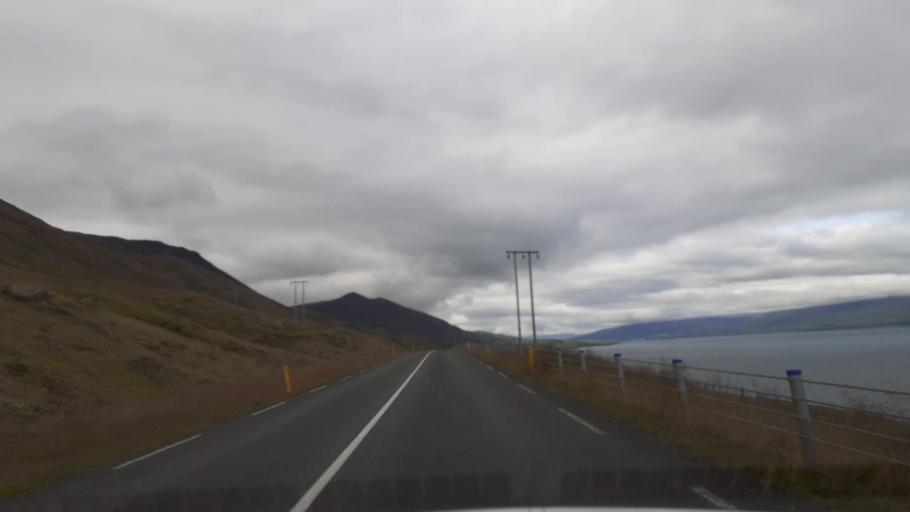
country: IS
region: Northeast
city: Akureyri
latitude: 65.8533
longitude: -18.0611
